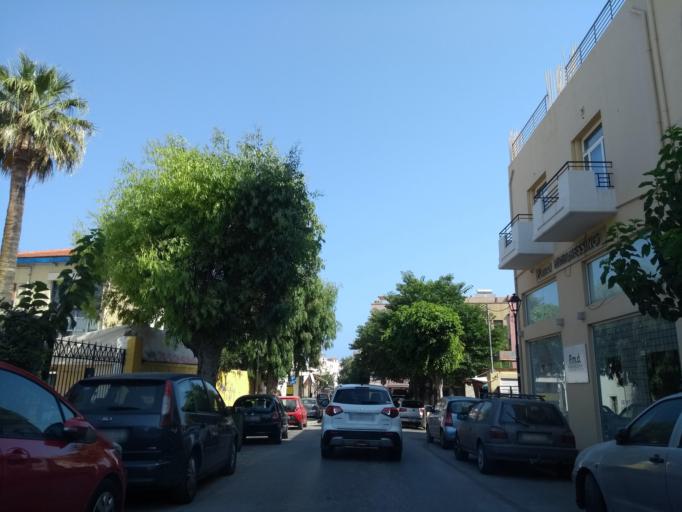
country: GR
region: Crete
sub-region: Nomos Chanias
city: Chania
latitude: 35.5149
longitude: 24.0221
